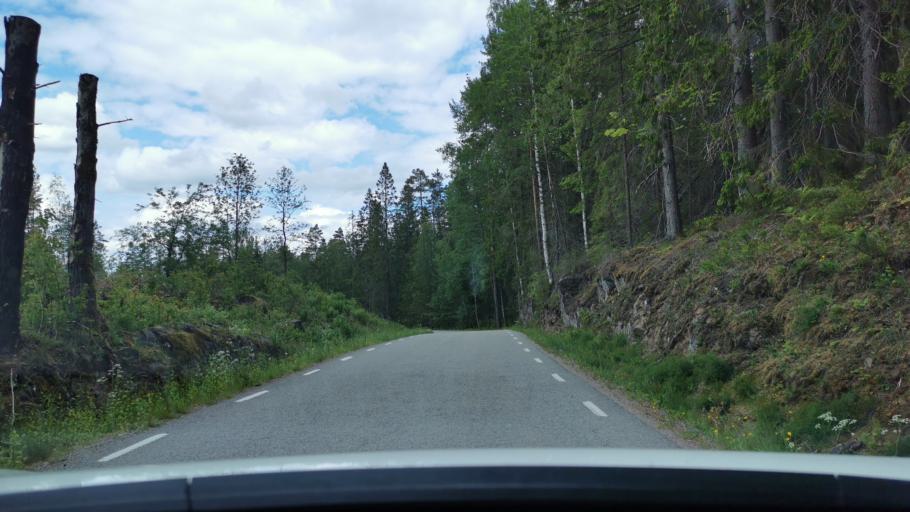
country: SE
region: Vaestra Goetaland
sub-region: Bengtsfors Kommun
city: Dals Langed
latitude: 58.8547
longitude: 12.3300
